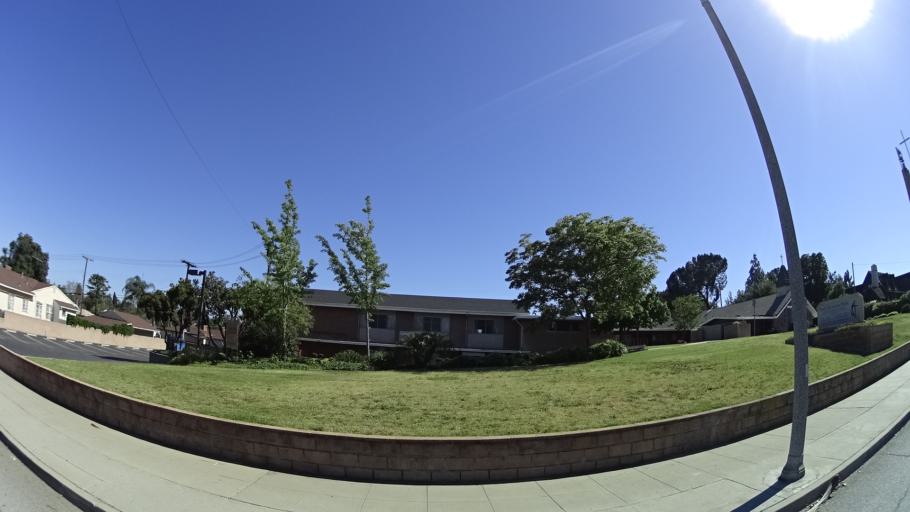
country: US
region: California
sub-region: Los Angeles County
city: Monterey Park
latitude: 34.0697
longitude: -118.1438
